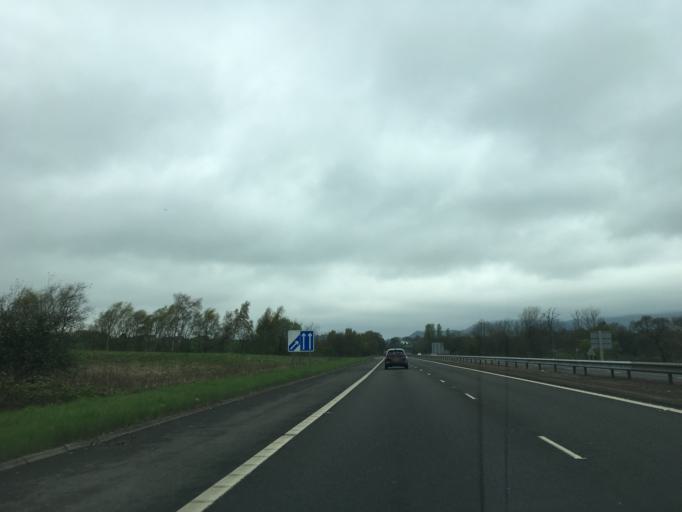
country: GB
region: Scotland
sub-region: Renfrewshire
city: Bishopton
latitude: 55.9016
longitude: -4.4856
